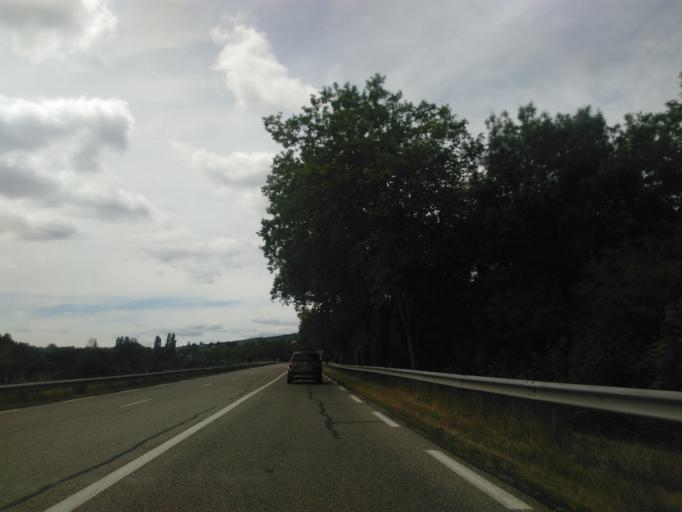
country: FR
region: Rhone-Alpes
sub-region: Departement de l'Ardeche
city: Villeneuve-de-Berg
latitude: 44.5904
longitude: 4.5511
